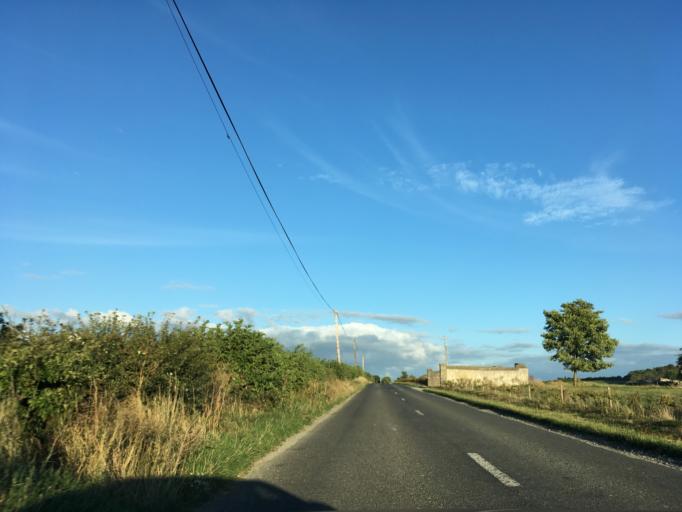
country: IE
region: Munster
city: Cashel
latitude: 52.4862
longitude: -7.9469
